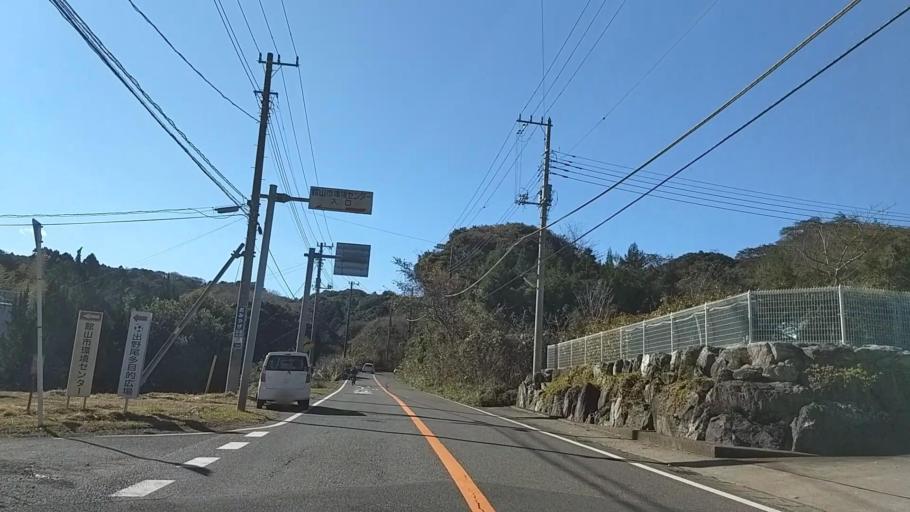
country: JP
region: Chiba
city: Tateyama
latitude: 34.9640
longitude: 139.8587
